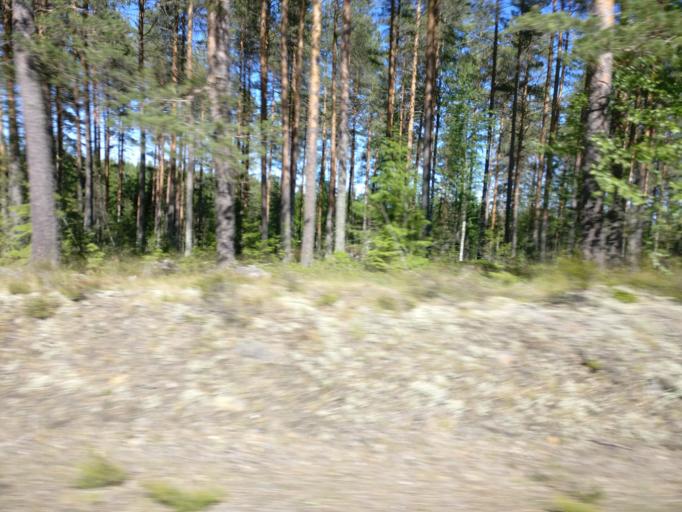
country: FI
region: Southern Savonia
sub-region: Savonlinna
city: Rantasalmi
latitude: 62.0971
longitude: 28.2708
